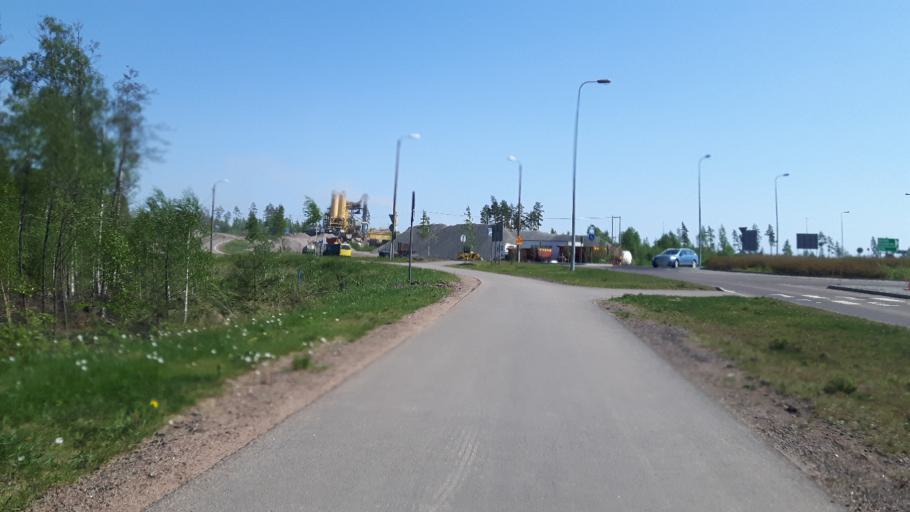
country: FI
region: Kymenlaakso
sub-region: Kotka-Hamina
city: Pyhtaeae
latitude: 60.4897
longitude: 26.5614
